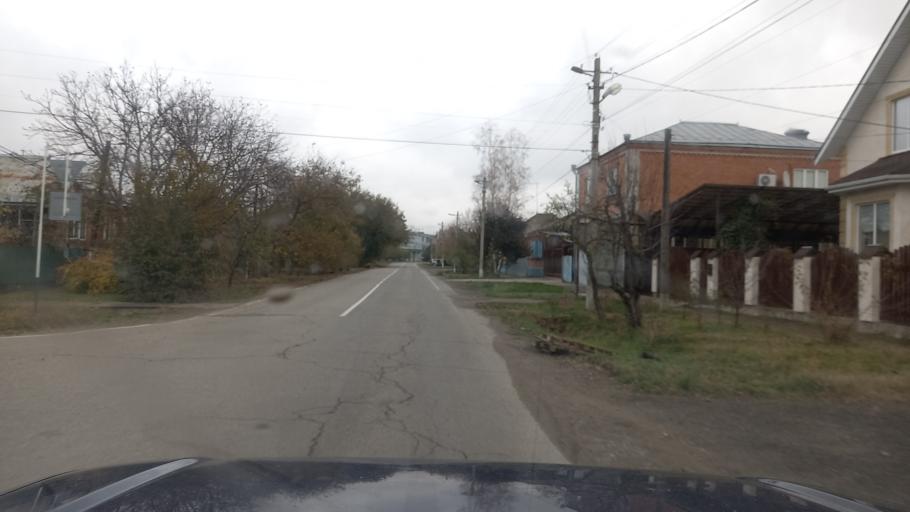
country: RU
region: Adygeya
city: Maykop
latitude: 44.6072
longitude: 40.0810
